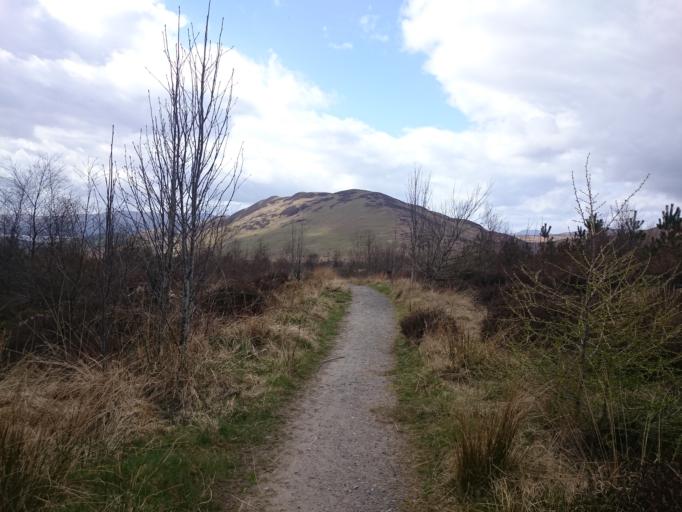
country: GB
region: Scotland
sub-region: Stirling
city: Killearn
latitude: 56.0952
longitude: -4.4900
